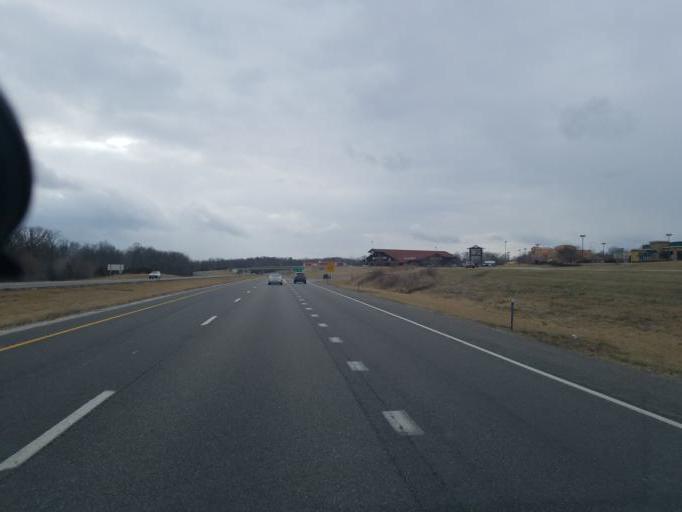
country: US
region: Missouri
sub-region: Boone County
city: Columbia
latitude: 38.9739
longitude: -92.2865
